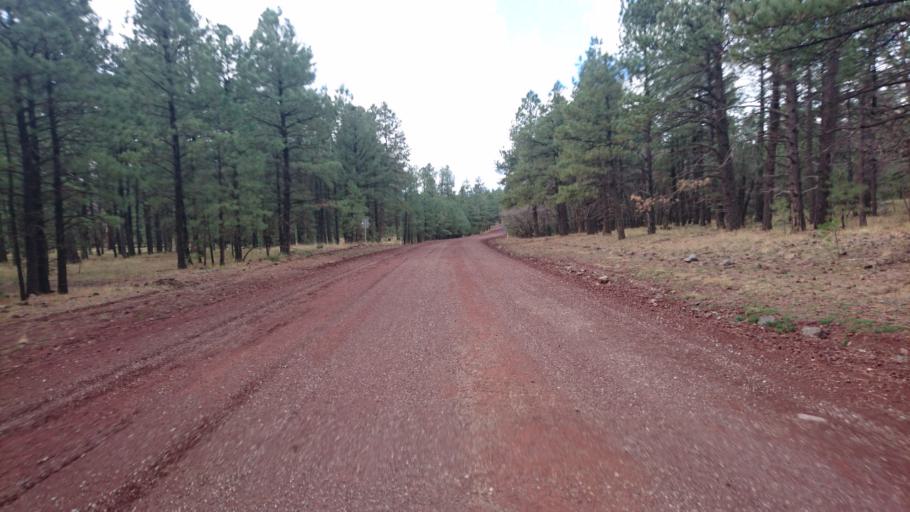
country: US
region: Arizona
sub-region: Coconino County
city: Parks
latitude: 35.2618
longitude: -111.9197
